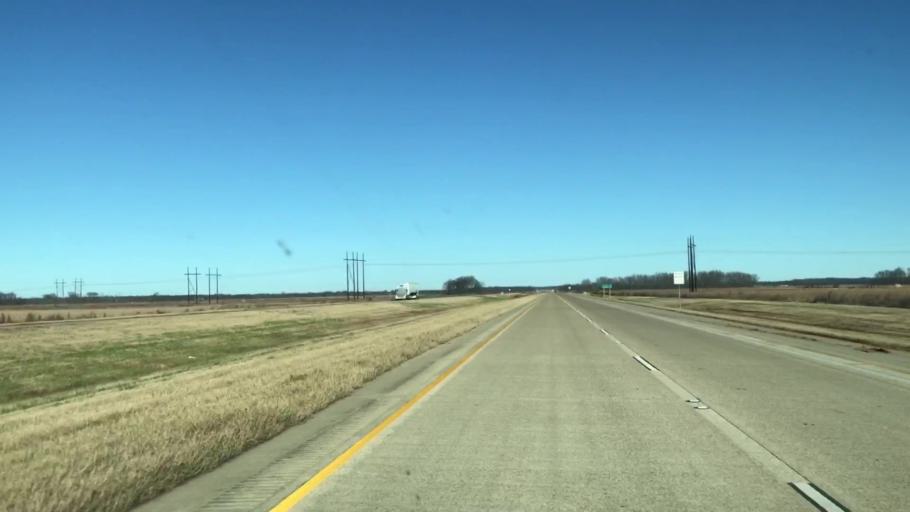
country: US
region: Louisiana
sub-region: Caddo Parish
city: Oil City
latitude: 32.7138
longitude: -93.8662
